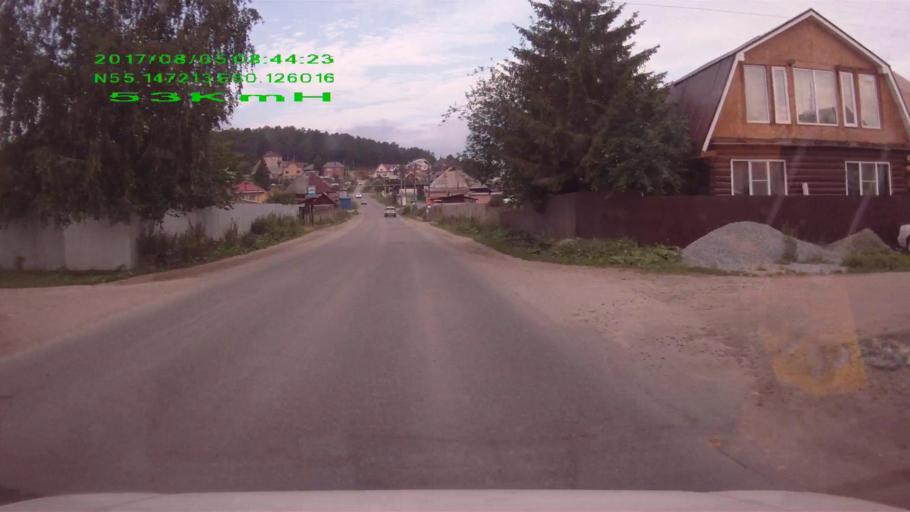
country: RU
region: Chelyabinsk
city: Turgoyak
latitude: 55.1472
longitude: 60.1257
